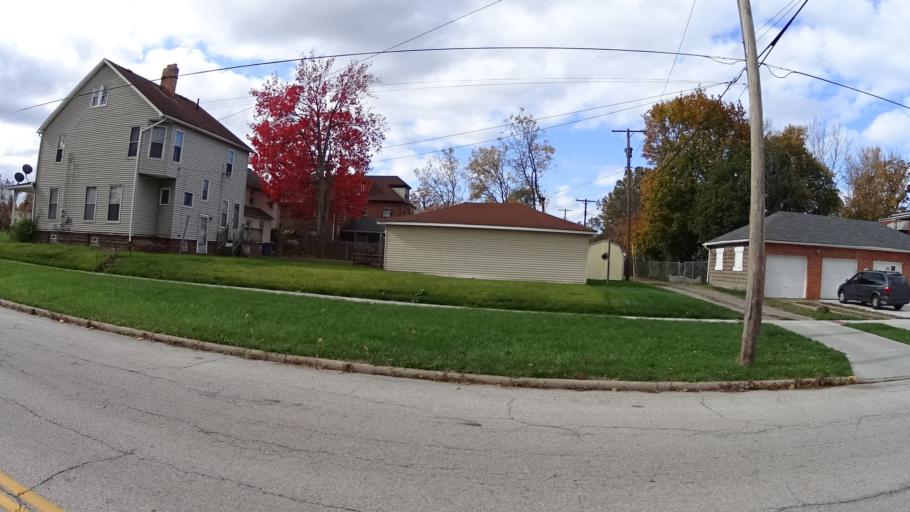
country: US
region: Ohio
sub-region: Lorain County
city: Sheffield
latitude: 41.4416
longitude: -82.1278
